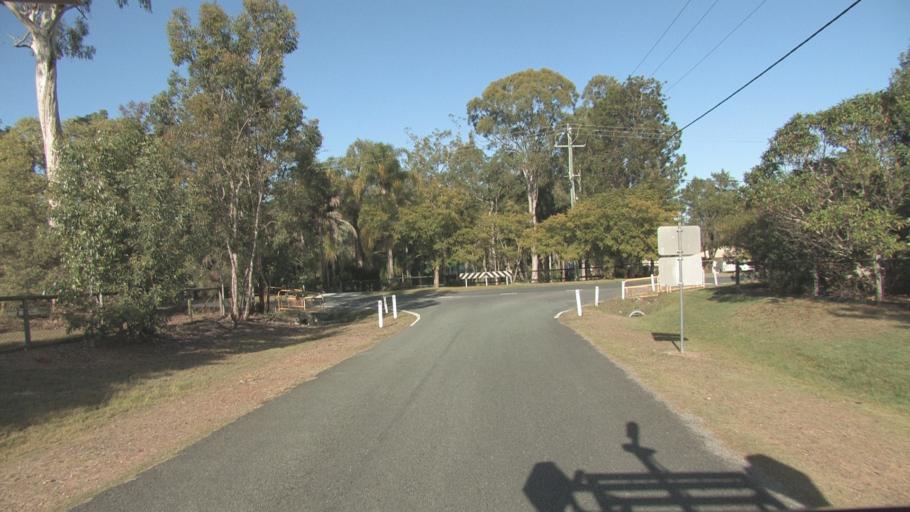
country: AU
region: Queensland
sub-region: Logan
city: Park Ridge South
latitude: -27.7371
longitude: 153.0310
